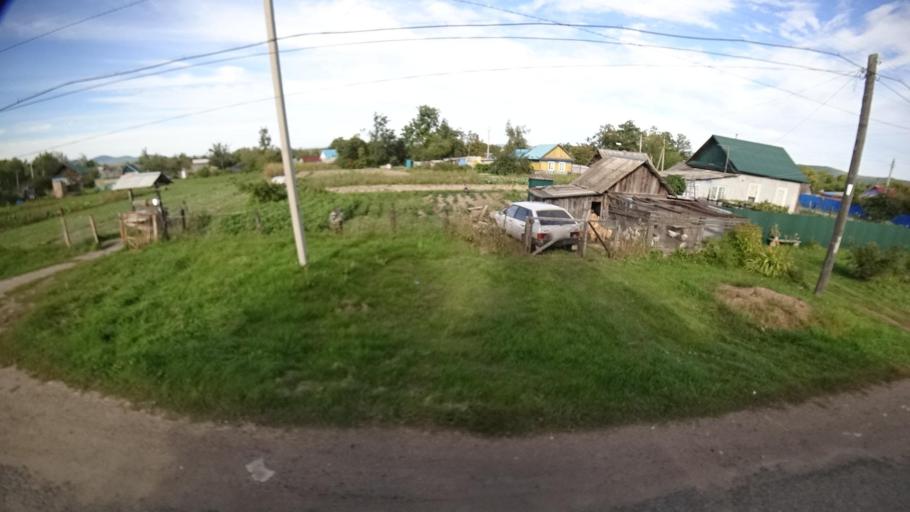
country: RU
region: Primorskiy
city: Dostoyevka
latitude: 44.3005
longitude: 133.4495
